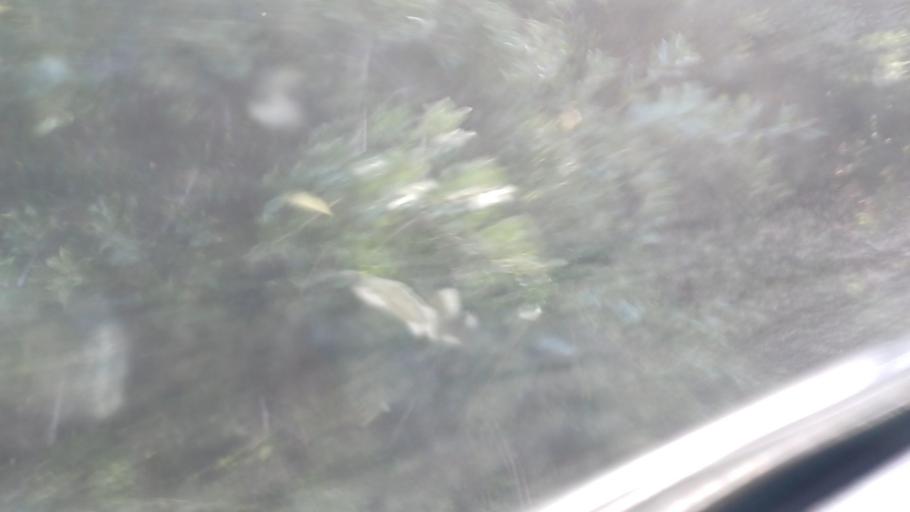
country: CY
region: Pafos
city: Mesogi
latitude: 34.8807
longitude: 32.5337
